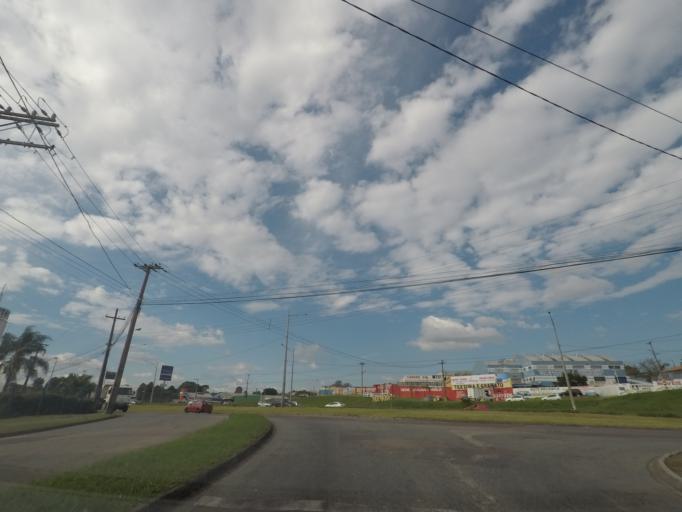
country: BR
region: Parana
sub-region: Sao Jose Dos Pinhais
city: Sao Jose dos Pinhais
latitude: -25.5347
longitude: -49.3015
